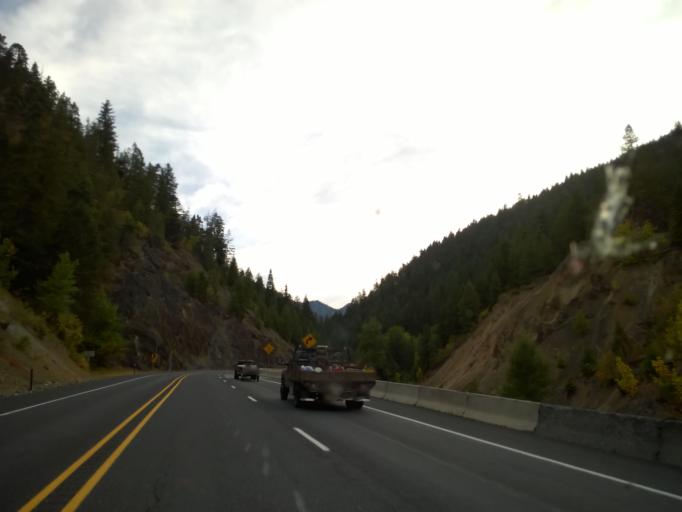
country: US
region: Washington
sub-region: Chelan County
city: Leavenworth
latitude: 47.4478
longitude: -120.6571
